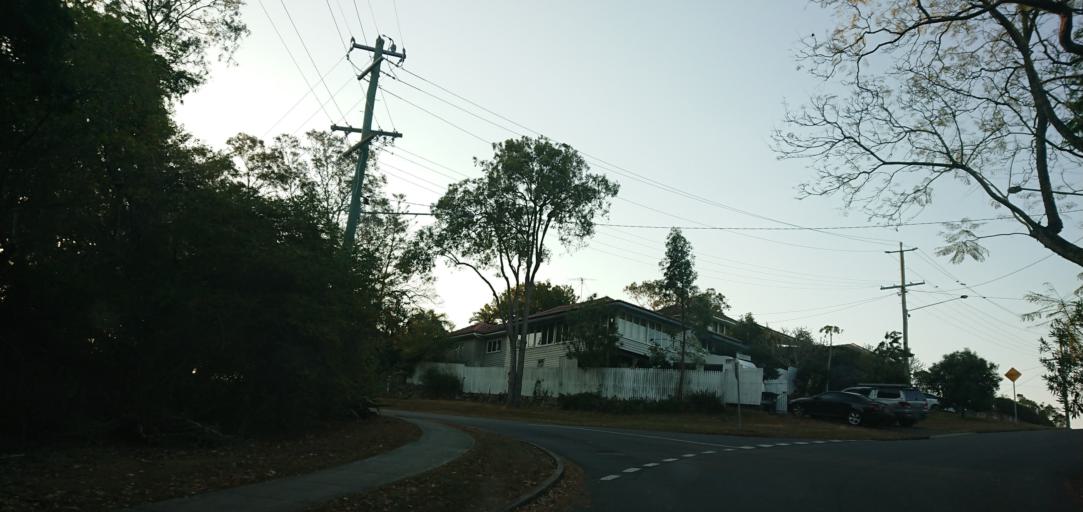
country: AU
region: Queensland
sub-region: Brisbane
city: Taringa
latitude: -27.5057
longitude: 152.9585
